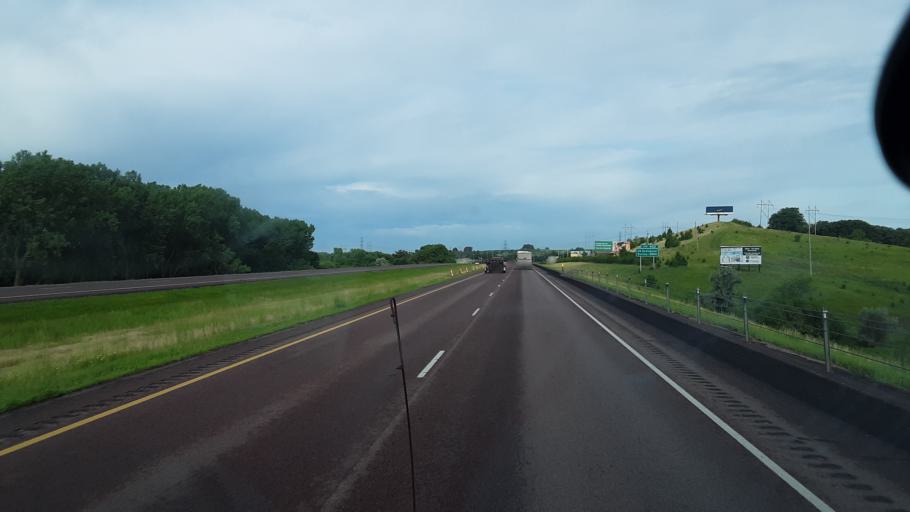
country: US
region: South Dakota
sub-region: Minnehaha County
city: Brandon
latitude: 43.6105
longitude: -96.6319
